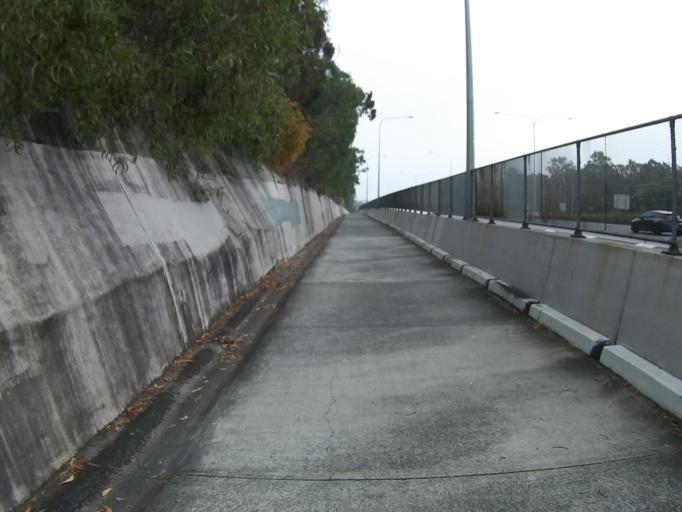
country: AU
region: Queensland
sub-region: Brisbane
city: Nathan
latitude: -27.5466
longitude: 153.0634
